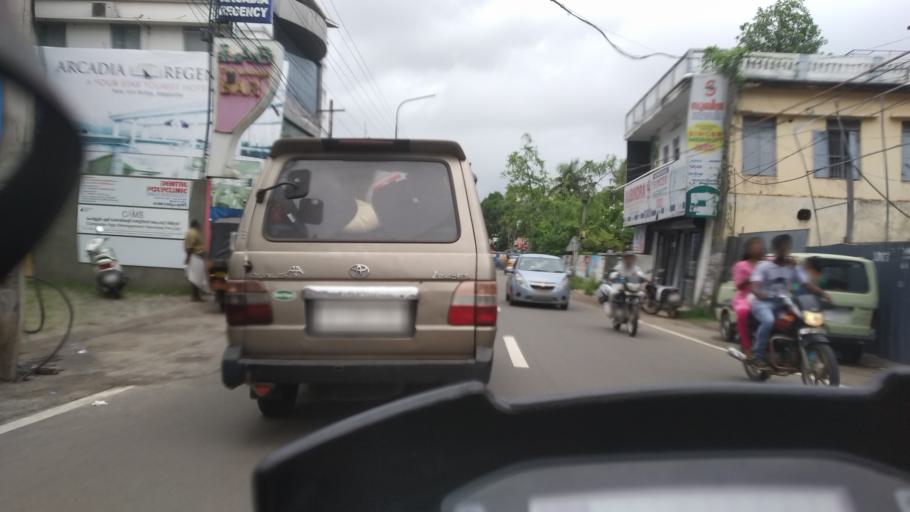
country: IN
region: Kerala
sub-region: Alappuzha
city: Alleppey
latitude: 9.4960
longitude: 76.3388
